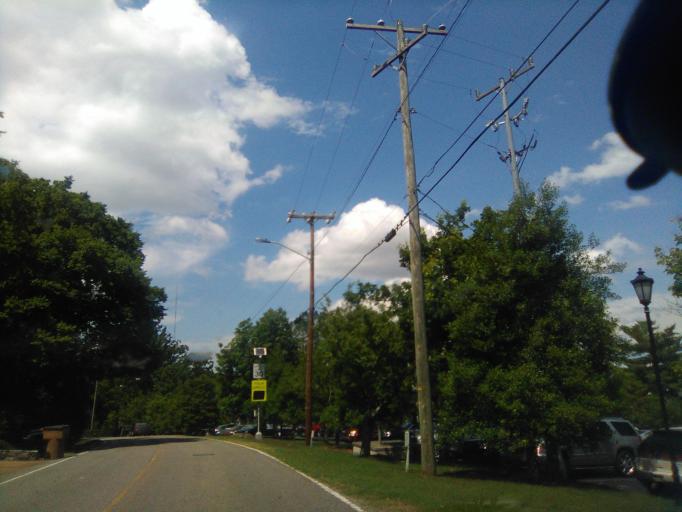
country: US
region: Tennessee
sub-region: Davidson County
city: Belle Meade
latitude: 36.1225
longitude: -86.8720
